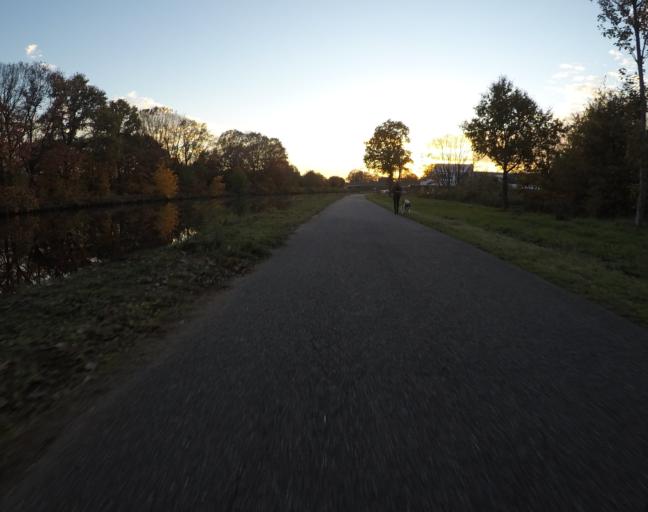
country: BE
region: Flanders
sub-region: Provincie Antwerpen
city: Herentals
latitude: 51.1723
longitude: 4.8515
